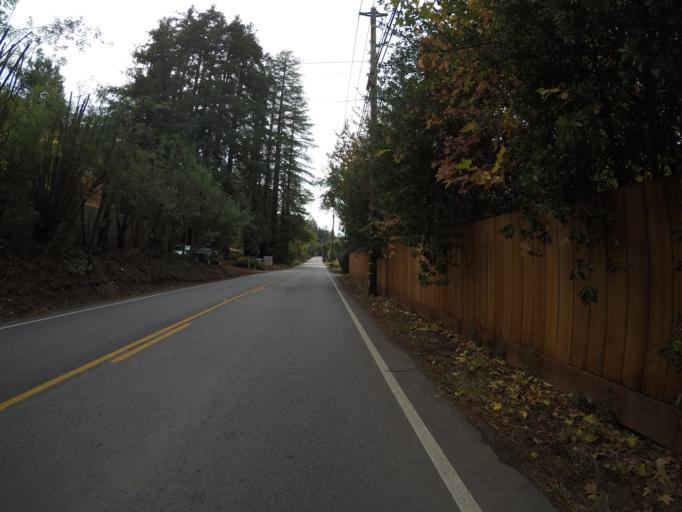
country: US
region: California
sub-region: Santa Cruz County
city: Scotts Valley
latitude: 37.0223
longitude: -121.9905
